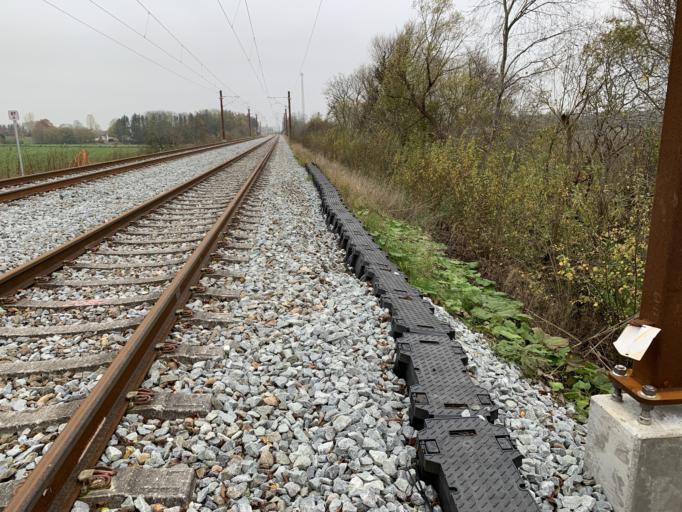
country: DK
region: Zealand
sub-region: Ringsted Kommune
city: Ringsted
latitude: 55.4143
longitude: 11.7510
